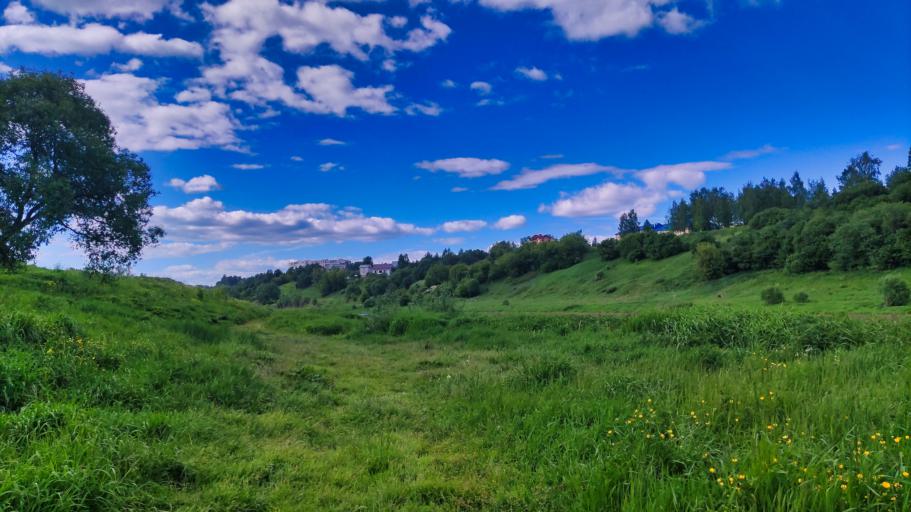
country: RU
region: Tverskaya
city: Rzhev
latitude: 56.2487
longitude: 34.3494
